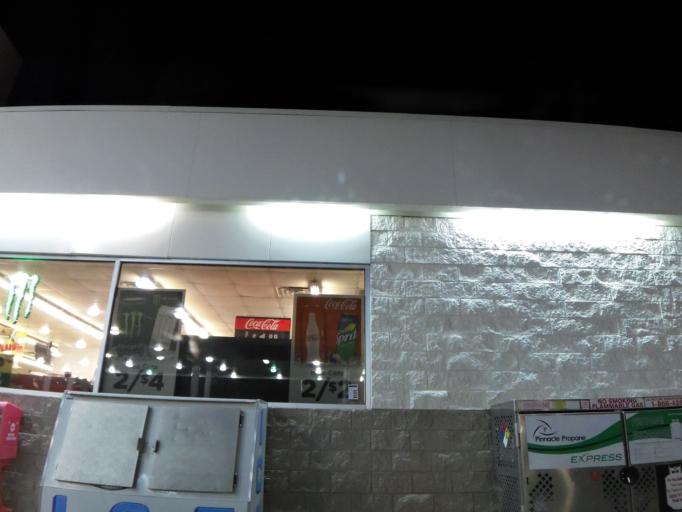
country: US
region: Alabama
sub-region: Marion County
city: Winfield
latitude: 33.9875
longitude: -87.7758
